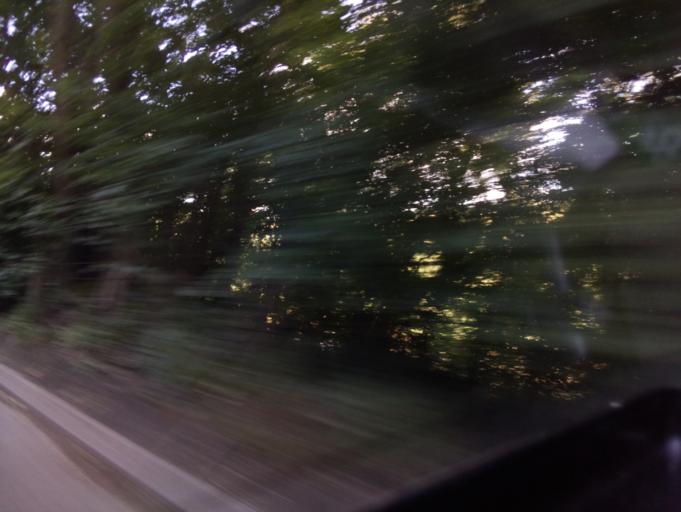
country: GB
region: England
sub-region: Herefordshire
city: Walford
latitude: 51.8719
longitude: -2.6055
